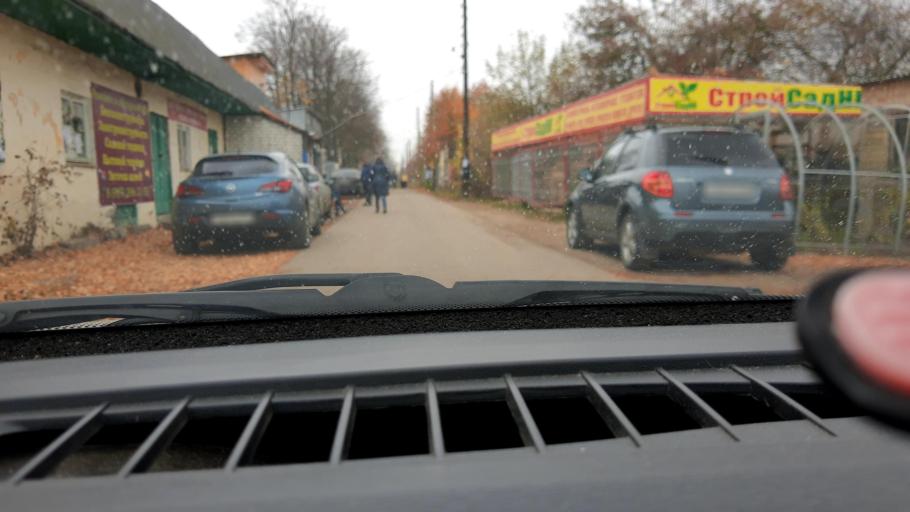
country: RU
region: Nizjnij Novgorod
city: Gorbatovka
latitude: 56.2587
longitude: 43.8403
